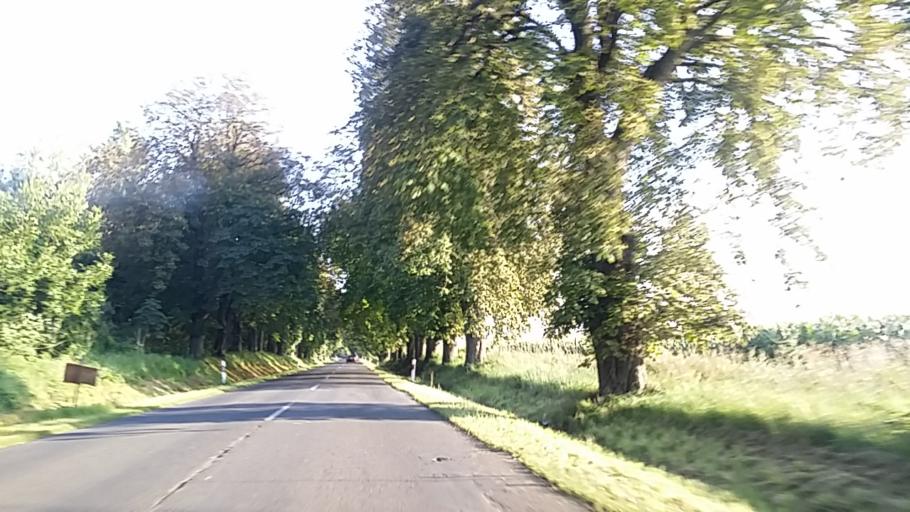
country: HU
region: Zala
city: Keszthely
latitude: 46.7307
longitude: 17.2403
